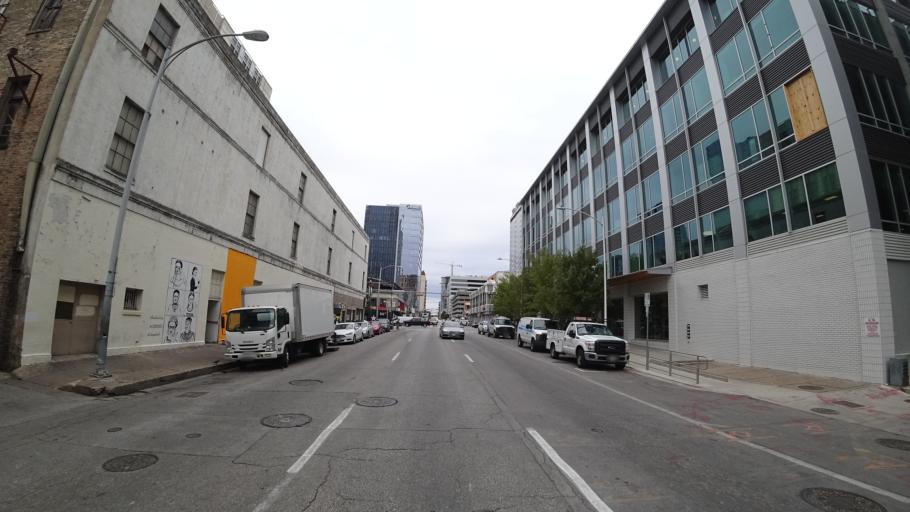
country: US
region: Texas
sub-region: Travis County
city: Austin
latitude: 30.2669
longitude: -97.7424
